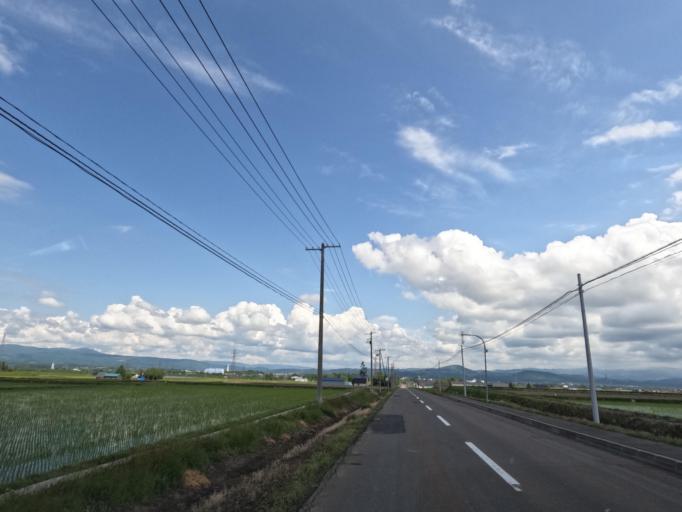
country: JP
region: Hokkaido
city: Takikawa
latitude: 43.5746
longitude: 141.8541
